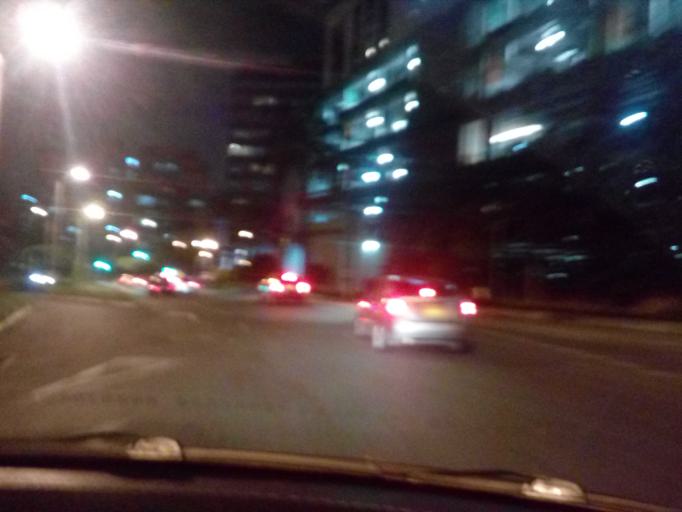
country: CO
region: Antioquia
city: Itagui
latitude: 6.1985
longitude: -75.5756
